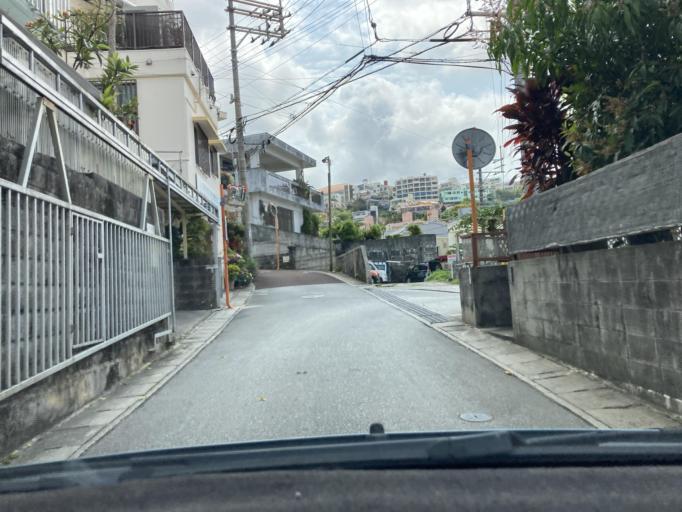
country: JP
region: Okinawa
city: Naha-shi
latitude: 26.2230
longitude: 127.7106
